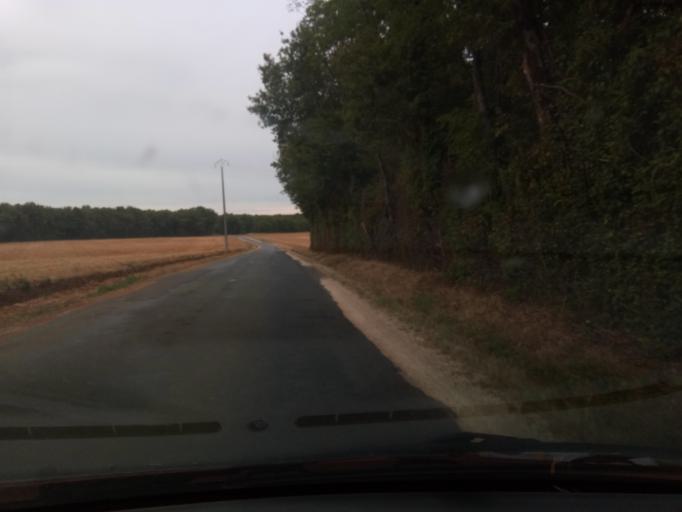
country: FR
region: Poitou-Charentes
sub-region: Departement de la Vienne
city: Saint-Savin
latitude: 46.5299
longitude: 0.7763
